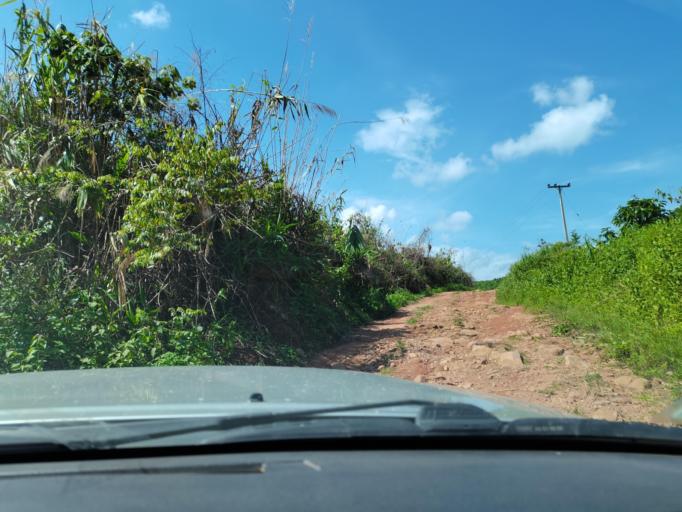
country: LA
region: Loungnamtha
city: Muang Nale
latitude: 20.5647
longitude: 101.0566
